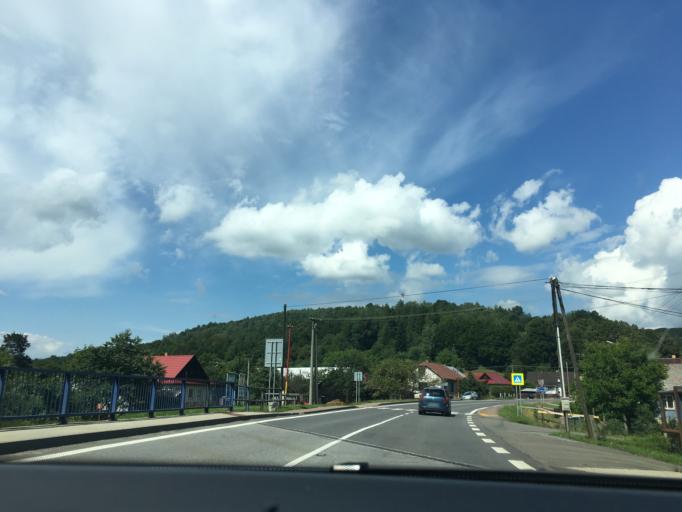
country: SK
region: Presovsky
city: Svidnik
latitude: 49.3589
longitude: 21.6507
